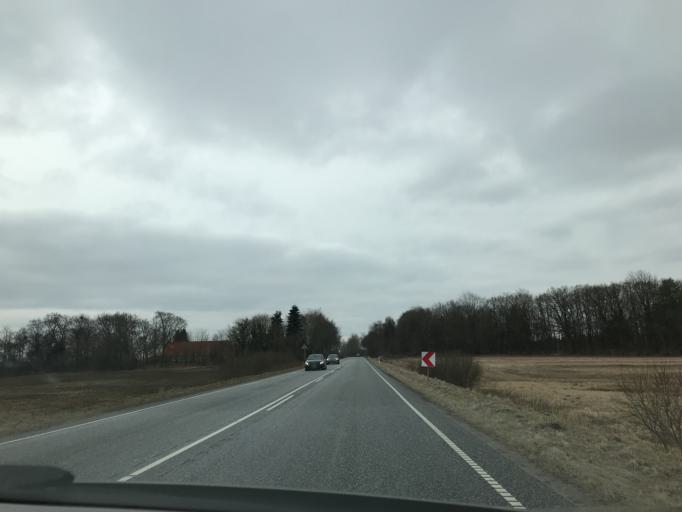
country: DK
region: South Denmark
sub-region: Varde Kommune
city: Olgod
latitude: 55.8444
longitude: 8.7124
